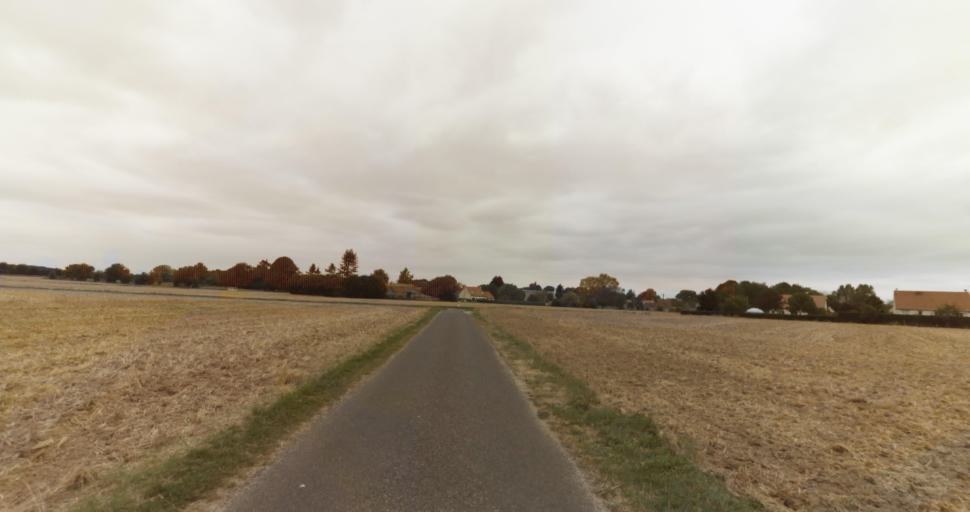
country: FR
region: Haute-Normandie
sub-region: Departement de l'Eure
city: La Couture-Boussey
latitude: 48.9271
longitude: 1.3223
